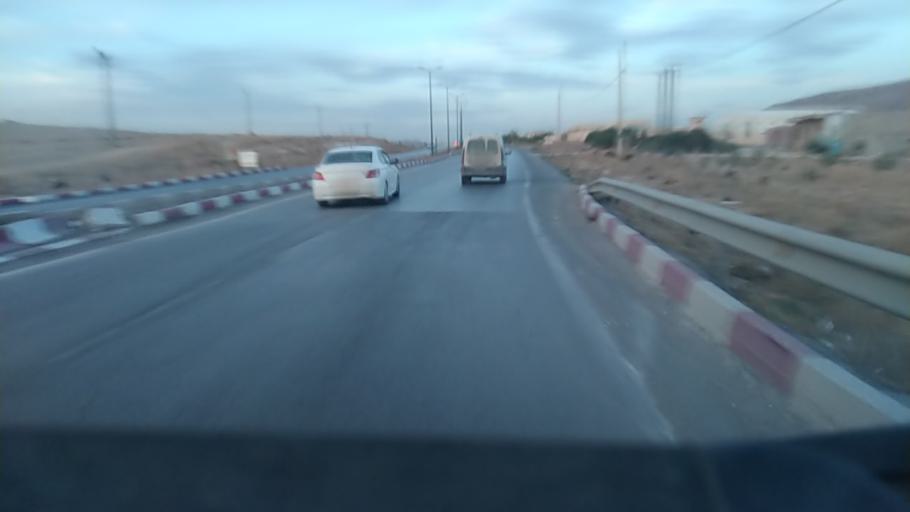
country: DZ
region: Oum el Bouaghi
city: Ain Kercha
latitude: 36.0807
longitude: 6.5900
